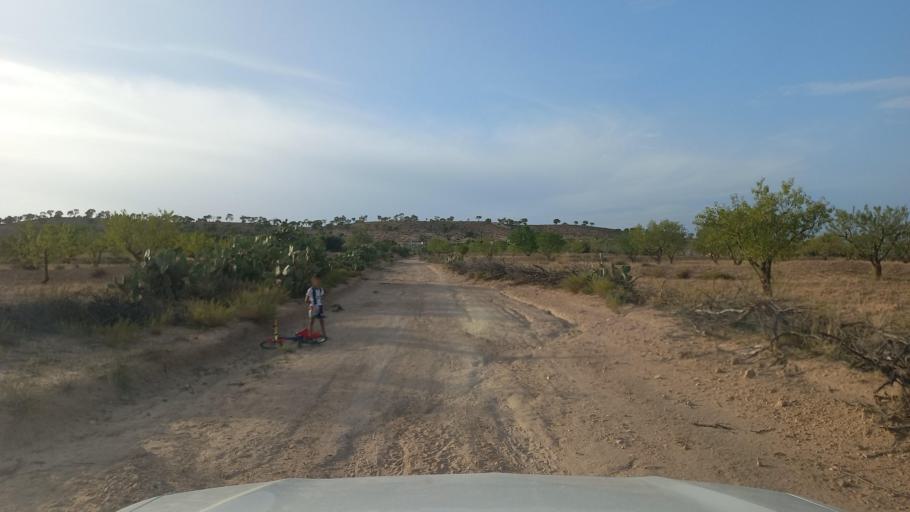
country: TN
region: Al Qasrayn
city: Sbiba
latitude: 35.4039
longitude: 8.8988
